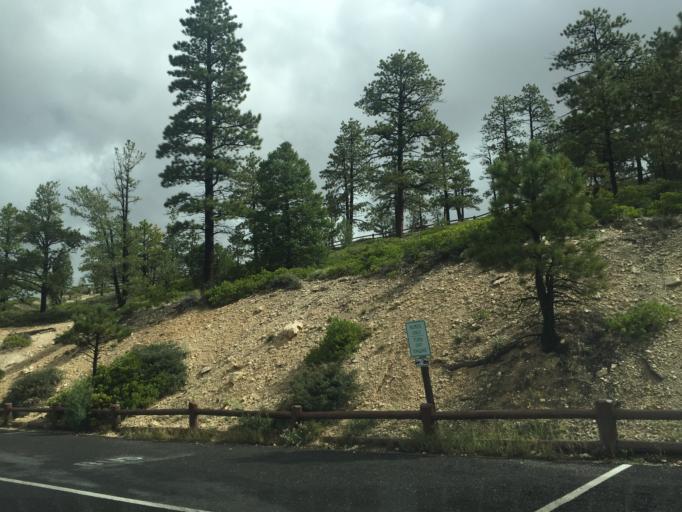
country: US
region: Utah
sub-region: Garfield County
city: Panguitch
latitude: 37.6147
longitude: -112.1707
